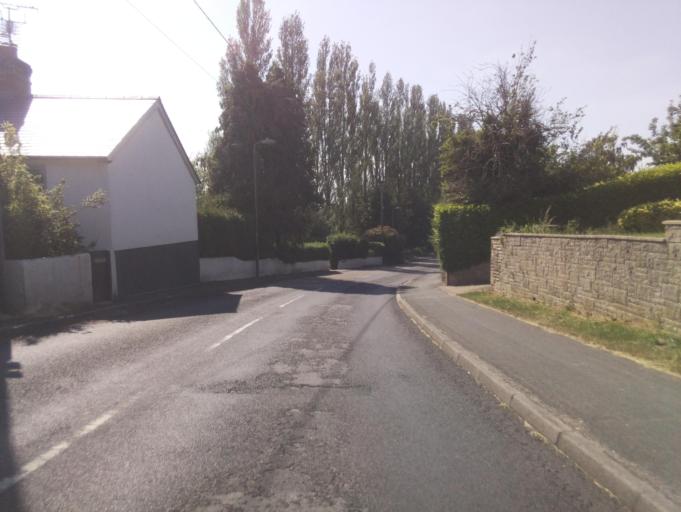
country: GB
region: England
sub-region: Hampshire
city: Andover
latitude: 51.2210
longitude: -1.5039
